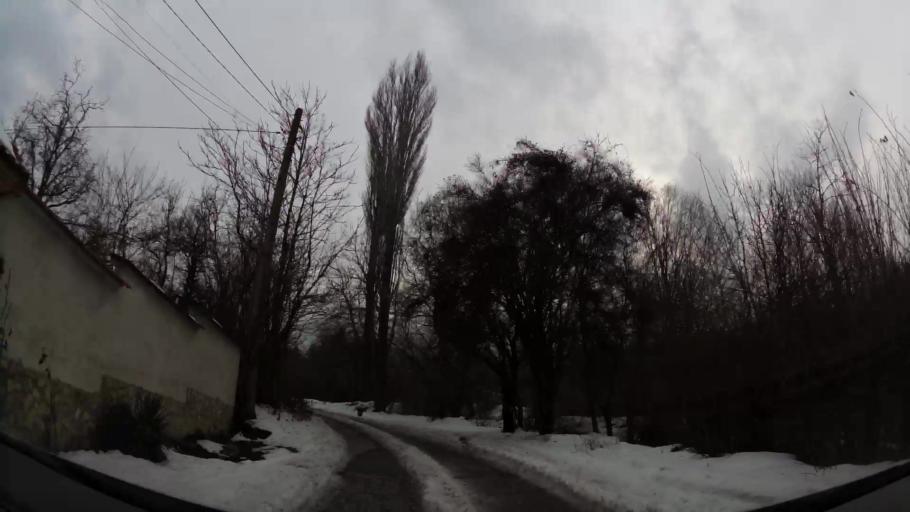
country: BG
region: Sofiya
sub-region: Obshtina Bozhurishte
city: Bozhurishte
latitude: 42.6511
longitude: 23.2311
